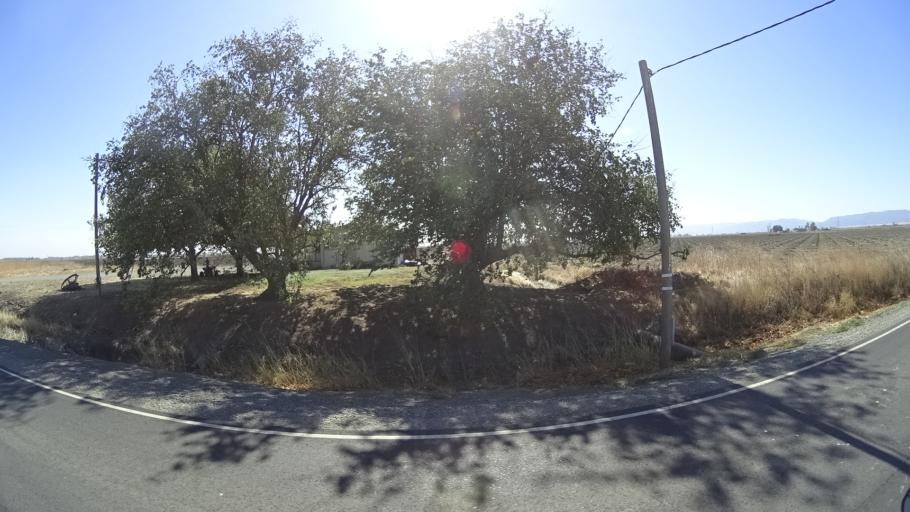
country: US
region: California
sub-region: Yolo County
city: Cottonwood
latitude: 38.6200
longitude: -121.9048
